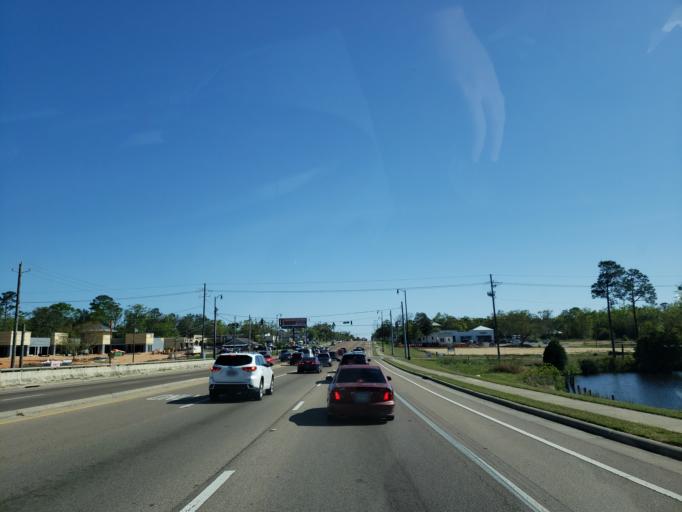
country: US
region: Mississippi
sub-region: Harrison County
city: West Gulfport
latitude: 30.4043
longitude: -89.0269
